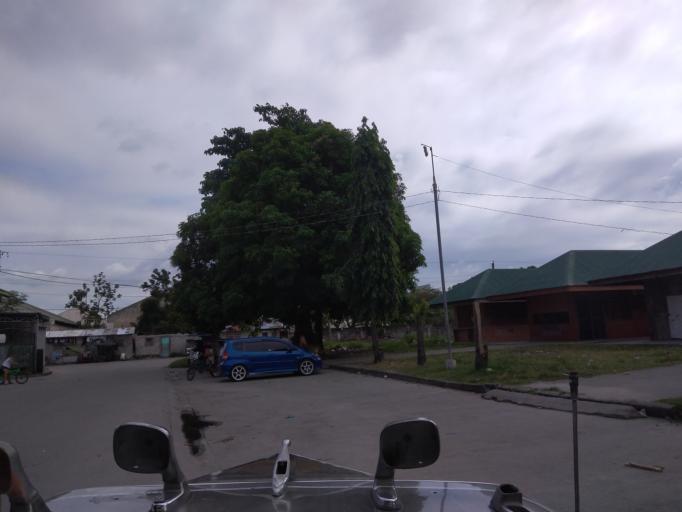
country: PH
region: Central Luzon
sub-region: Province of Pampanga
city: Pandacaqui
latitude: 15.1821
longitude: 120.6433
